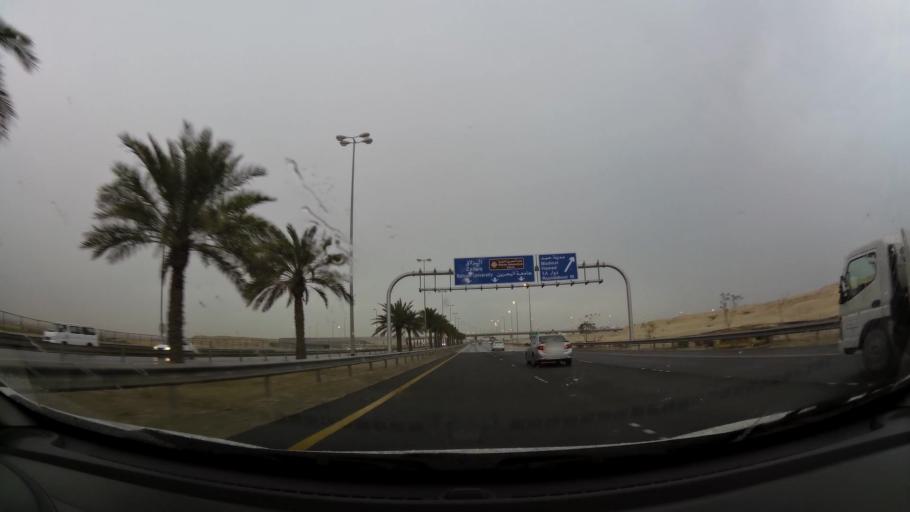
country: BH
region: Central Governorate
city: Dar Kulayb
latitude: 26.0860
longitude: 50.5153
